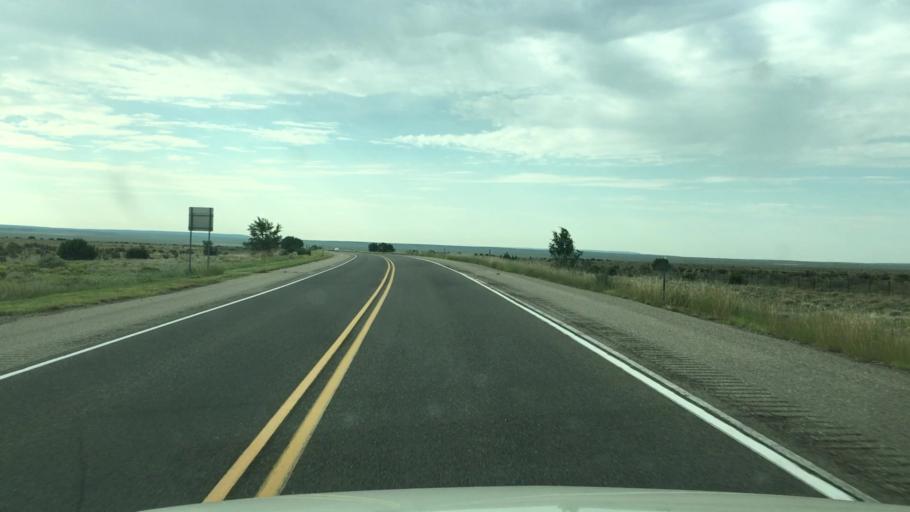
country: US
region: New Mexico
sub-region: Santa Fe County
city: Eldorado at Santa Fe
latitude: 35.2202
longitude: -105.8003
